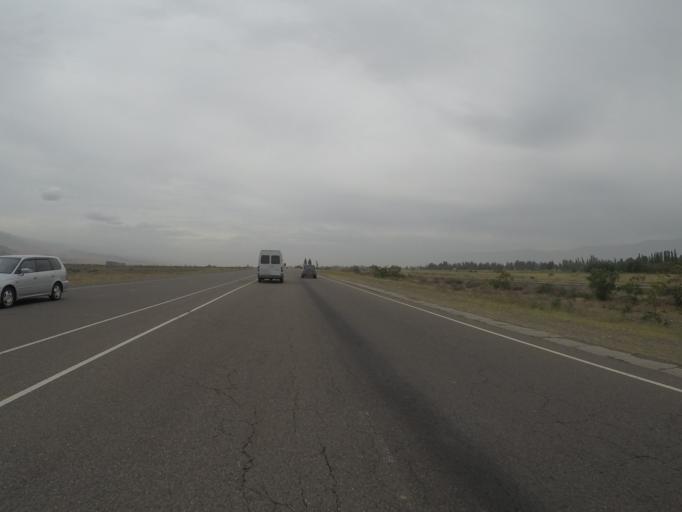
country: KG
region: Chuy
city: Bystrovka
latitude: 42.8291
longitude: 75.5281
